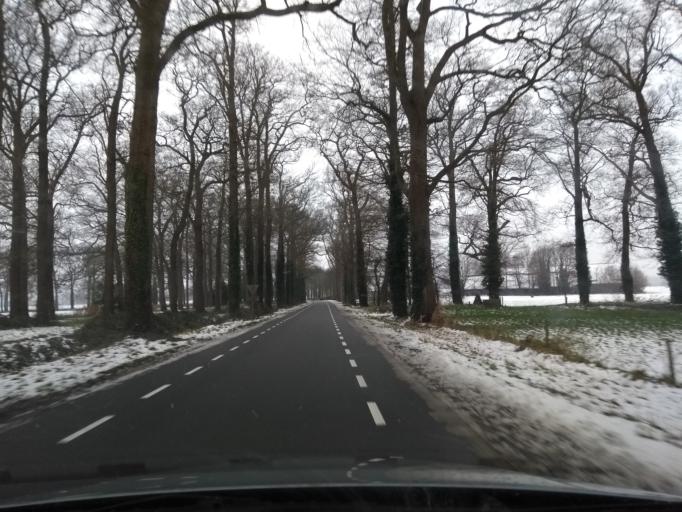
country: NL
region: Gelderland
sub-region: Gemeente Lochem
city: Barchem
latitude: 52.1605
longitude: 6.4554
